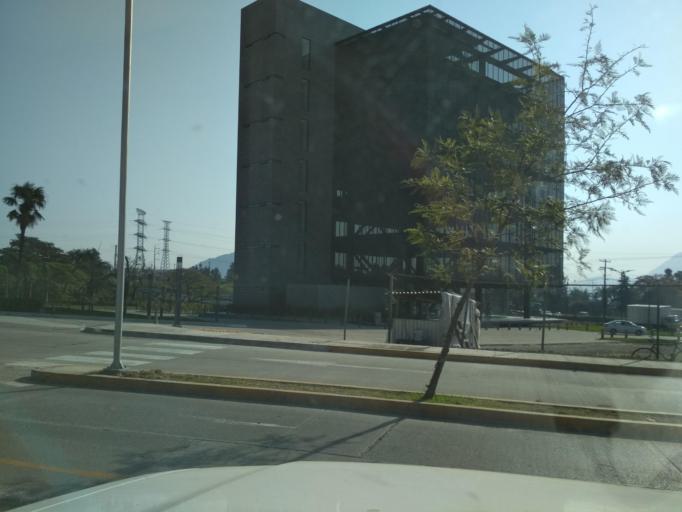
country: MX
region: Veracruz
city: Ixtac Zoquitlan
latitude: 18.8595
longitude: -97.0708
